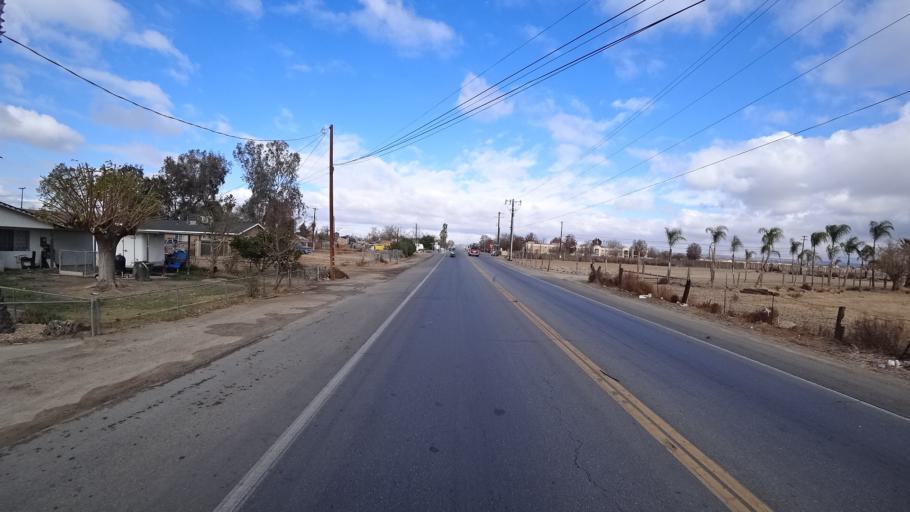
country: US
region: California
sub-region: Kern County
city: Bakersfield
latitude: 35.3386
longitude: -118.9855
